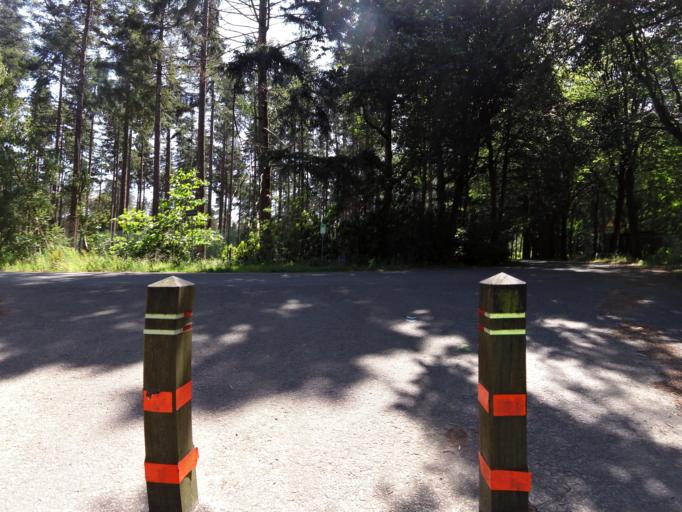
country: BE
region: Flanders
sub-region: Provincie West-Vlaanderen
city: Zedelgem
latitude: 51.1695
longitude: 3.1582
